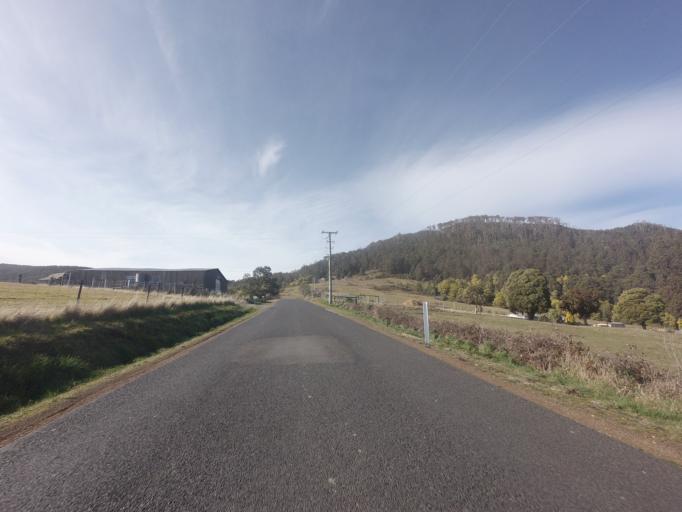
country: AU
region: Tasmania
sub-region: Kingborough
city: Kettering
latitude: -43.1703
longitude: 147.1720
